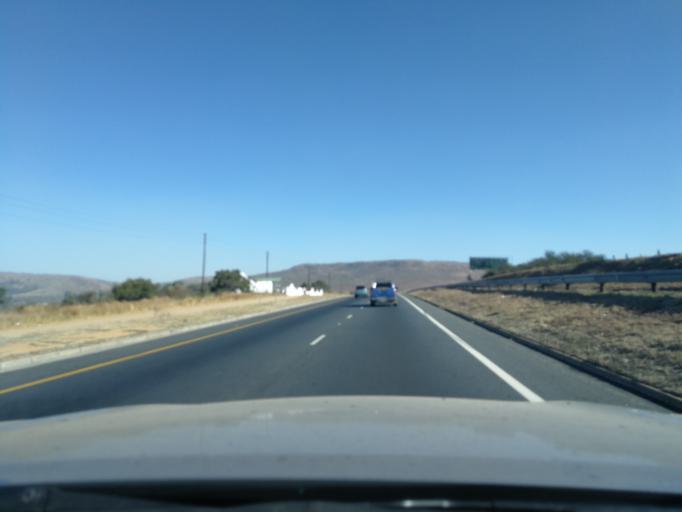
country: ZA
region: Gauteng
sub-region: West Rand District Municipality
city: Muldersdriseloop
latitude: -26.0522
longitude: 27.8383
